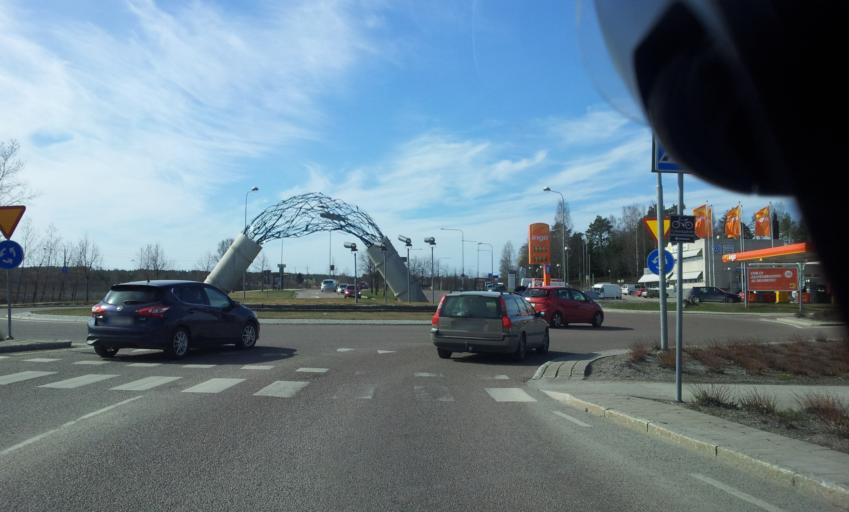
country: SE
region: Gaevleborg
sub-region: Hudiksvalls Kommun
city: Hudiksvall
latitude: 61.7176
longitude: 17.0956
